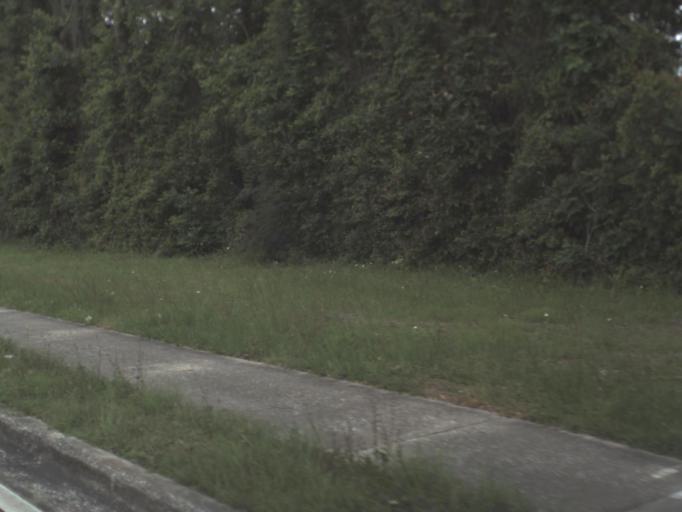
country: US
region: Florida
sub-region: Columbia County
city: Lake City
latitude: 30.1641
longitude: -82.6383
